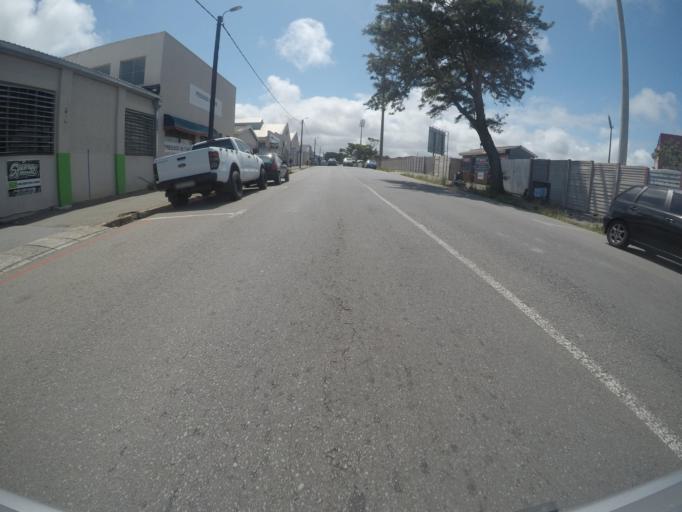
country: ZA
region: Eastern Cape
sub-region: Buffalo City Metropolitan Municipality
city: East London
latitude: -33.0088
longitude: 27.9063
